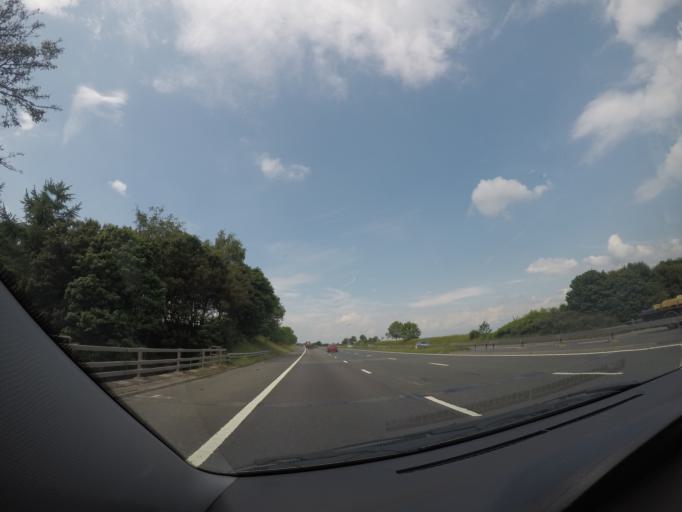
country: GB
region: England
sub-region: Cumbria
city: Scotby
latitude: 54.7819
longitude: -2.8565
